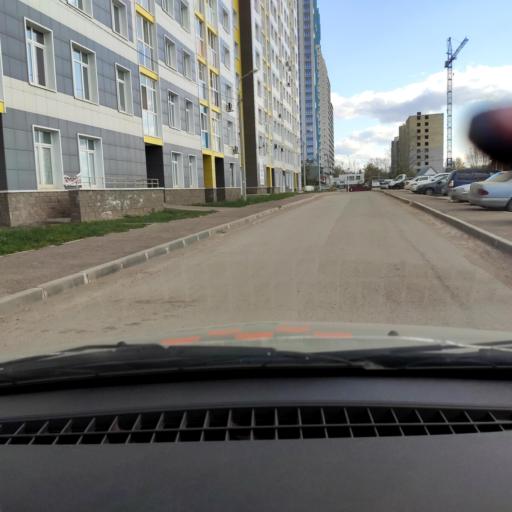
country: RU
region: Bashkortostan
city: Ufa
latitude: 54.6845
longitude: 55.9822
